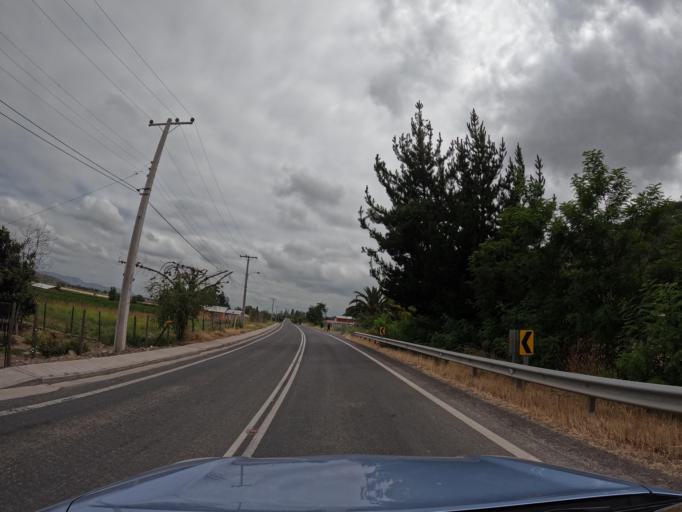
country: CL
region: Maule
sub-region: Provincia de Curico
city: Teno
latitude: -34.7877
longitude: -71.2291
